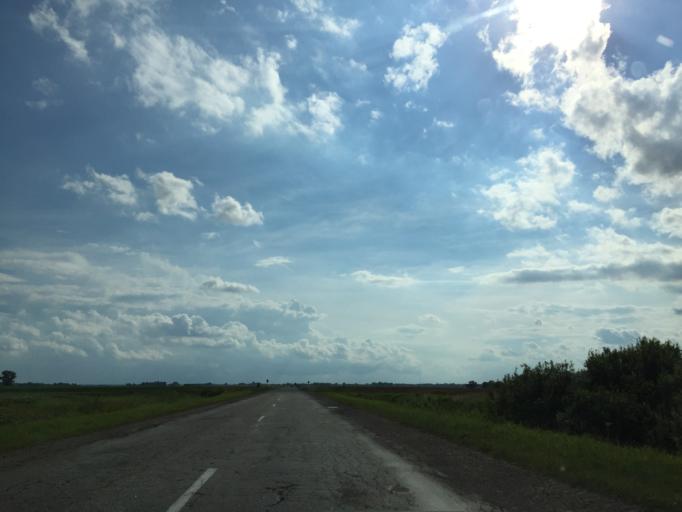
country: LV
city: Tervete
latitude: 56.5797
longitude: 23.4396
